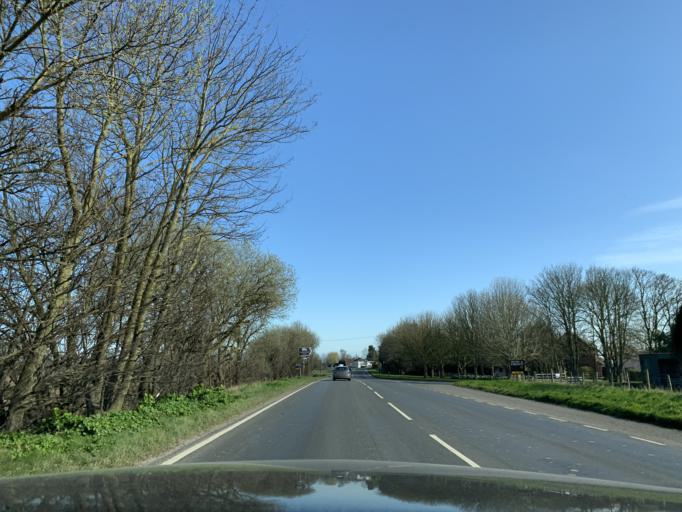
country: GB
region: England
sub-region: Kent
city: Romney Marsh
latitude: 50.9908
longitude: 0.8934
